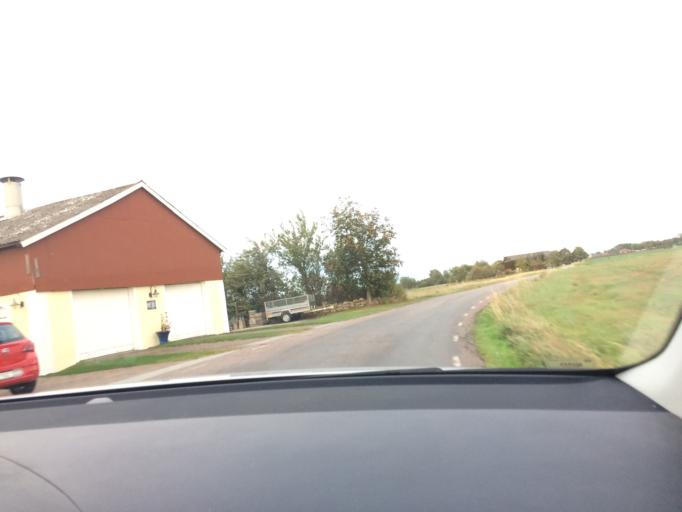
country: SE
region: Skane
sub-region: Hoors Kommun
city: Loberod
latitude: 55.7852
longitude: 13.4408
